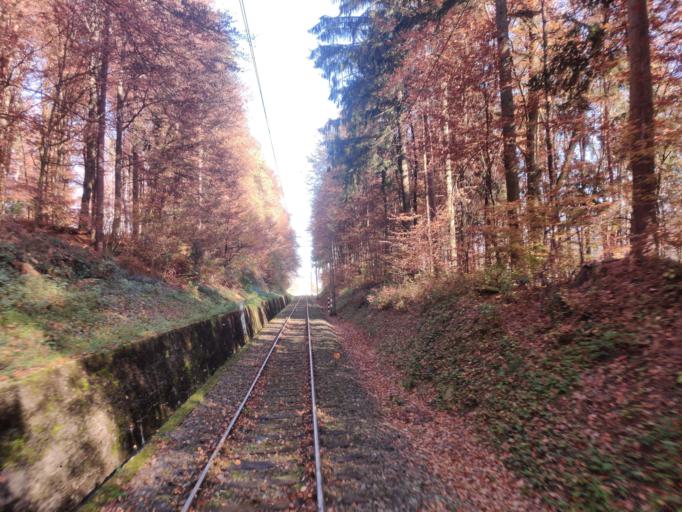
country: AT
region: Styria
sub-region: Politischer Bezirk Suedoststeiermark
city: Feldbach
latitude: 46.9394
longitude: 15.8775
